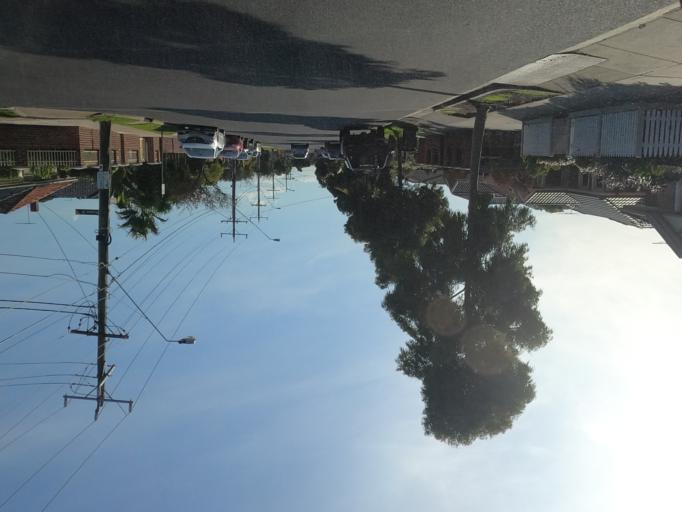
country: AU
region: Victoria
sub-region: Moonee Valley
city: Airport West
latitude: -37.7219
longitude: 144.8822
